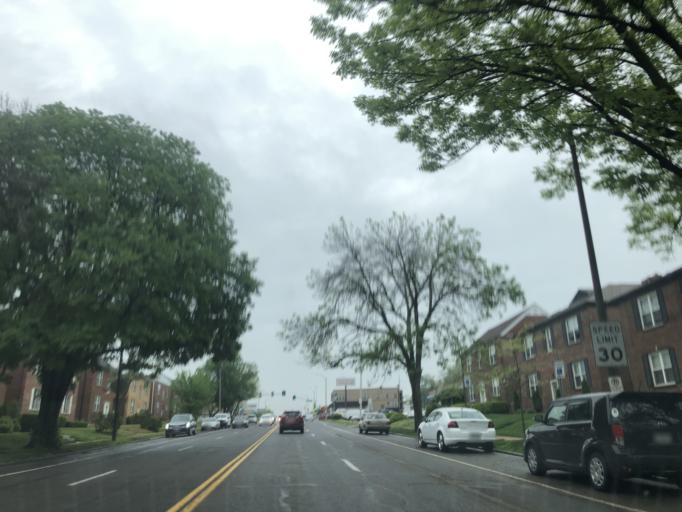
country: US
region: Missouri
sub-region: Saint Louis County
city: Shrewsbury
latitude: 38.5880
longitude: -90.3110
